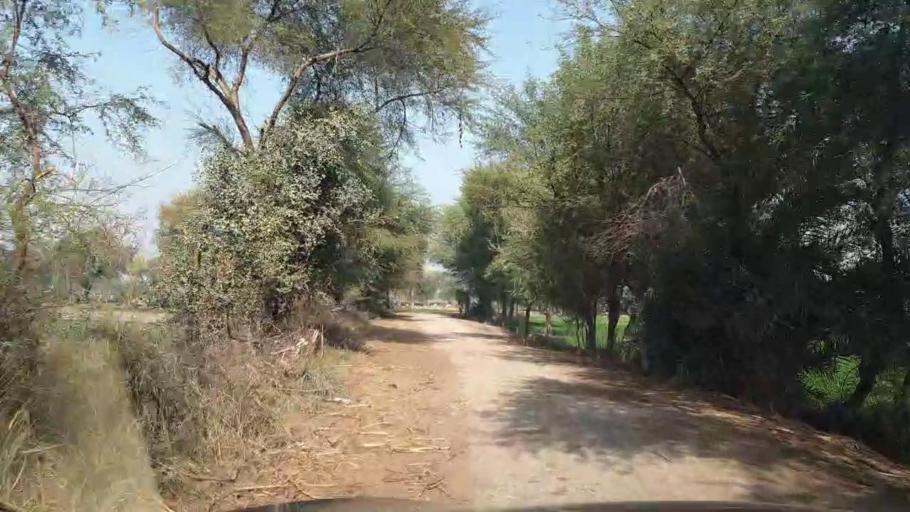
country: PK
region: Sindh
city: Ubauro
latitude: 28.1109
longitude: 69.7738
